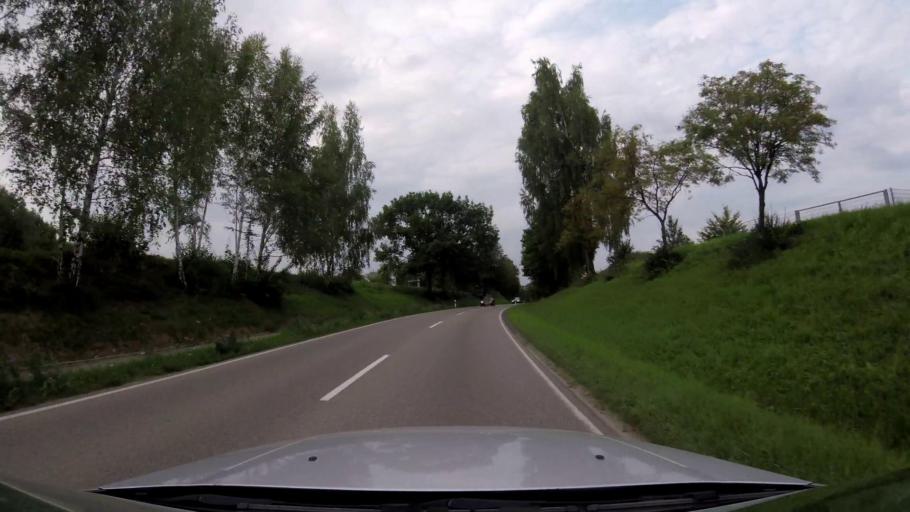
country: DE
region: Baden-Wuerttemberg
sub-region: Regierungsbezirk Stuttgart
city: Allmersbach im Tal
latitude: 48.9124
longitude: 9.4649
